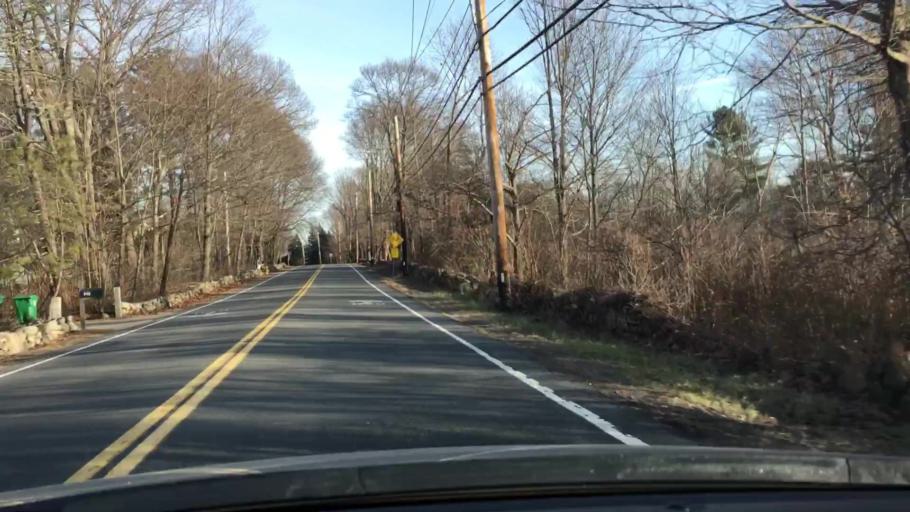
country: US
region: Massachusetts
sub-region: Norfolk County
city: Westwood
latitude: 42.2213
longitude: -71.2077
